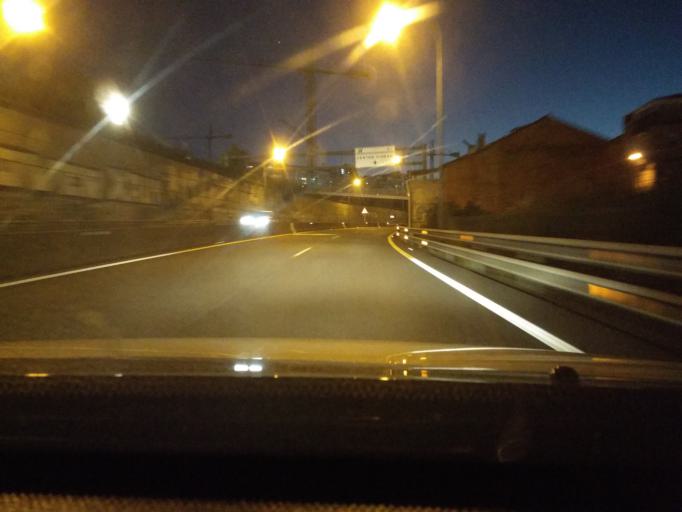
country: ES
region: Galicia
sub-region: Provincia de Pontevedra
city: Vigo
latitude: 42.2373
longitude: -8.7090
